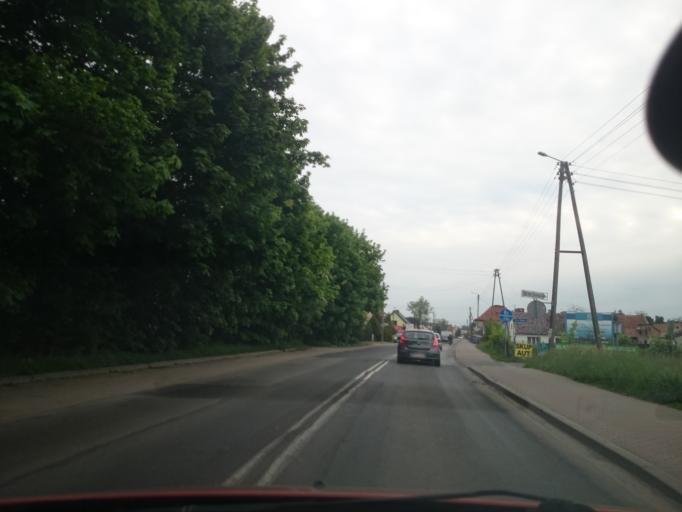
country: PL
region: Opole Voivodeship
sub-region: Powiat opolski
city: Dobrzen Wielki
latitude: 50.7684
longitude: 17.8477
